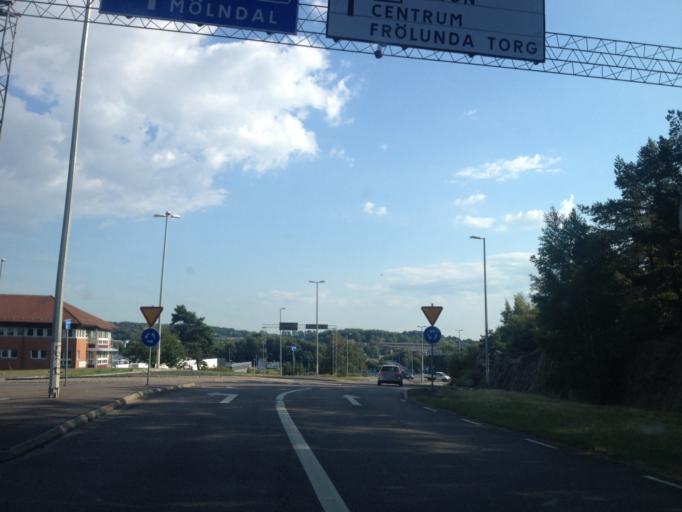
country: SE
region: Vaestra Goetaland
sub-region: Goteborg
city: Majorna
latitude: 57.6499
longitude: 11.9399
